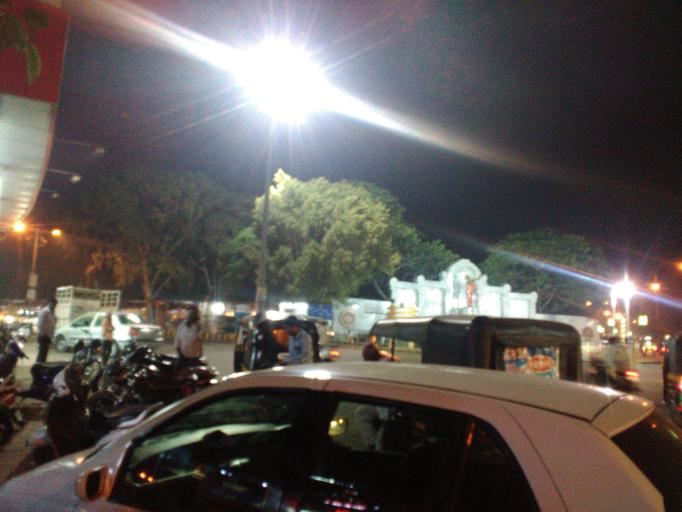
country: IN
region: Maharashtra
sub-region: Solapur
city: Solapur
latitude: 17.6702
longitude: 75.9012
